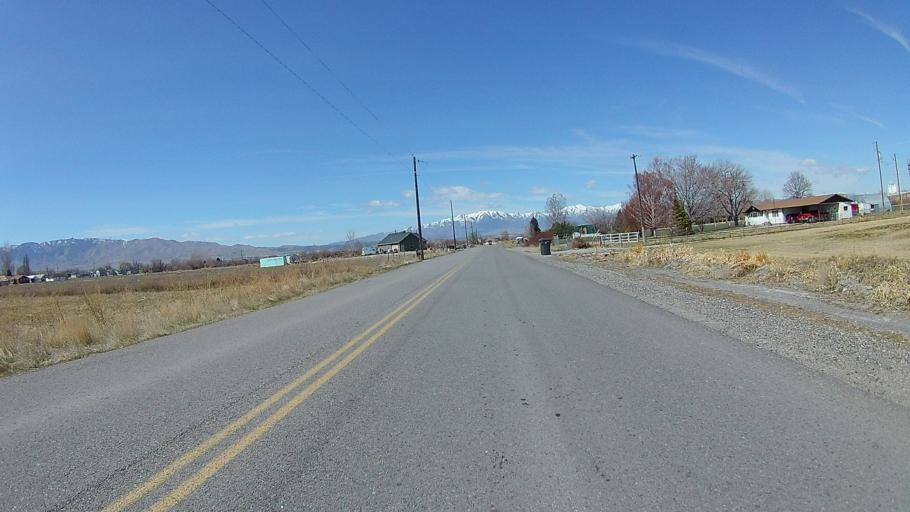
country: US
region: Utah
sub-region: Utah County
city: Lehi
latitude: 40.3728
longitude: -111.8277
